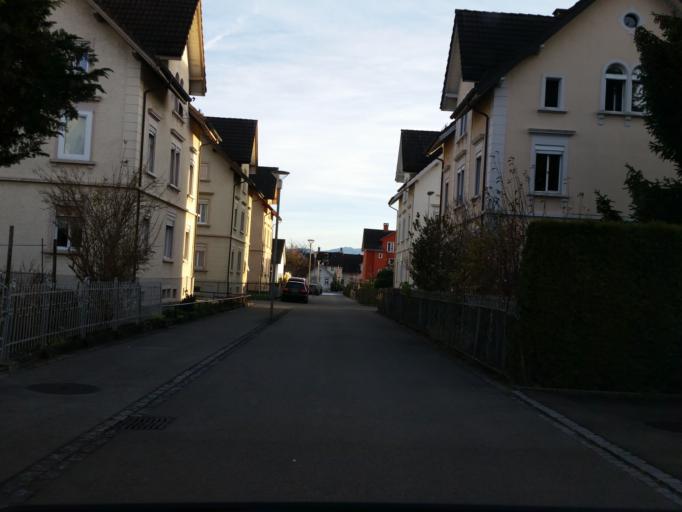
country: CH
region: Thurgau
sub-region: Arbon District
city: Romanshorn
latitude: 47.5618
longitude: 9.3743
